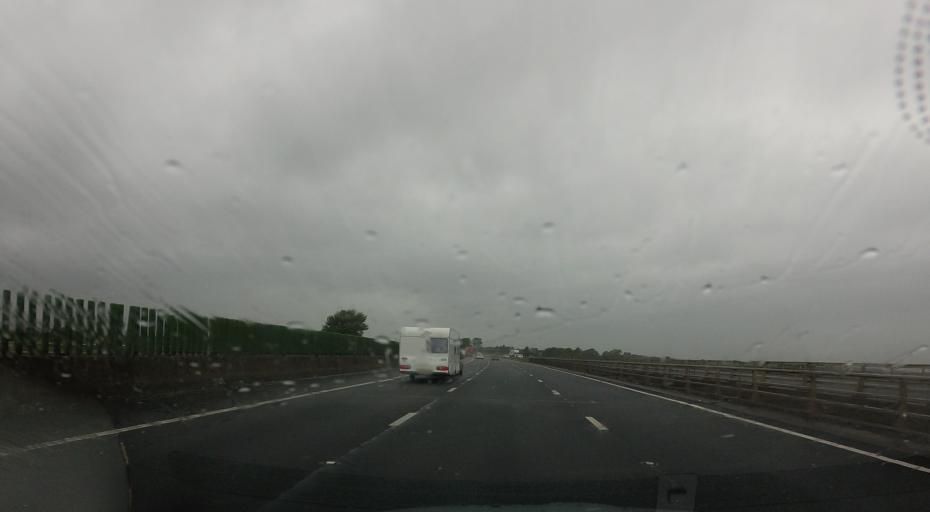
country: GB
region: Scotland
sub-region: Dumfries and Galloway
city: Gretna
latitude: 54.9748
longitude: -3.0094
